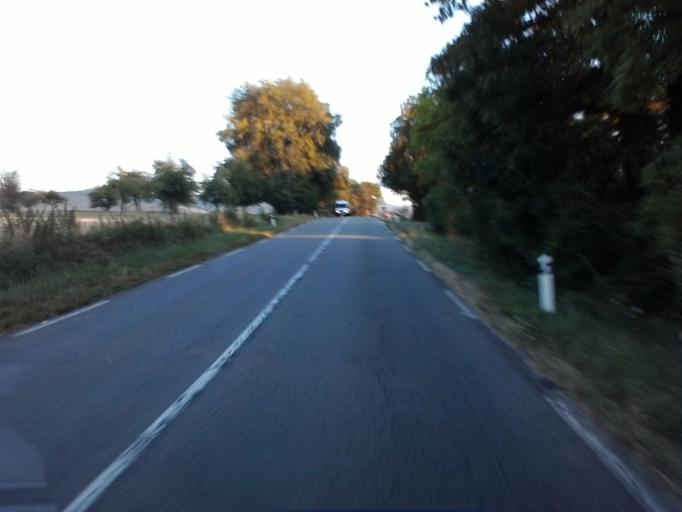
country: FR
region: Franche-Comte
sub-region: Departement du Doubs
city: Quingey
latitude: 47.0744
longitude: 5.8824
